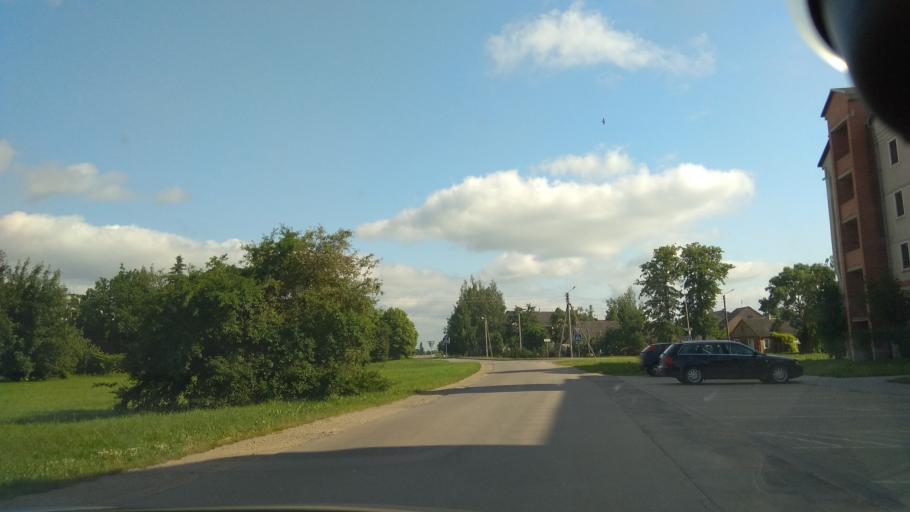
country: LT
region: Siauliu apskritis
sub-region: Joniskis
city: Joniskis
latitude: 56.2422
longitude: 23.6284
